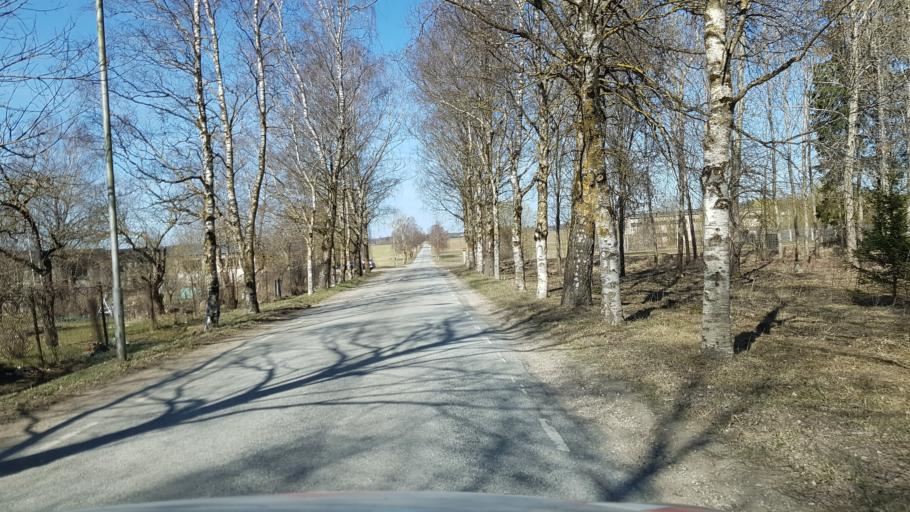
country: EE
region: Laeaene-Virumaa
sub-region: Vinni vald
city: Vinni
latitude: 59.2948
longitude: 26.4263
